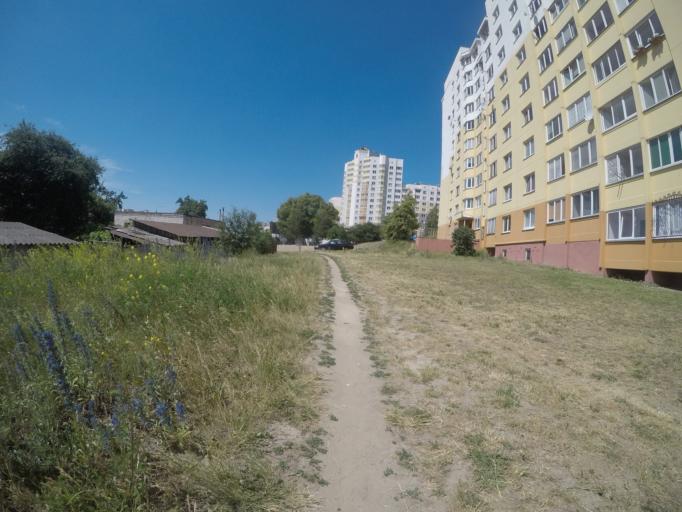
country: BY
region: Grodnenskaya
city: Hrodna
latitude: 53.6959
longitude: 23.8411
